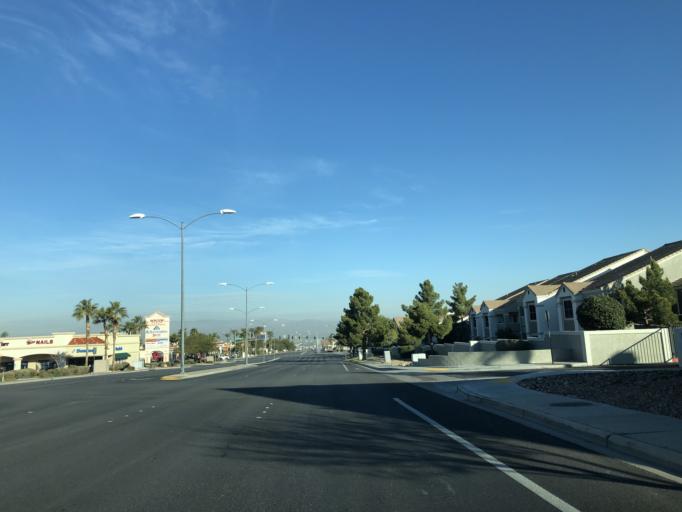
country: US
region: Nevada
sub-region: Clark County
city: Whitney
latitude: 36.0196
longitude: -115.0472
